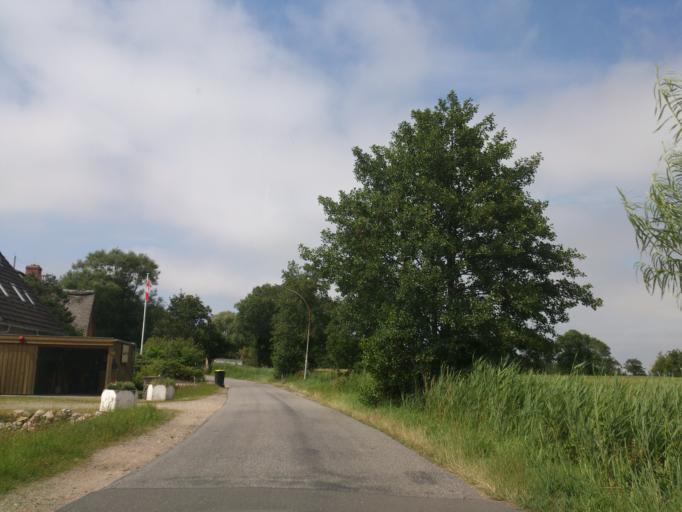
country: DE
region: Schleswig-Holstein
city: Sankt Peter-Ording
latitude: 54.3174
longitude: 8.6221
